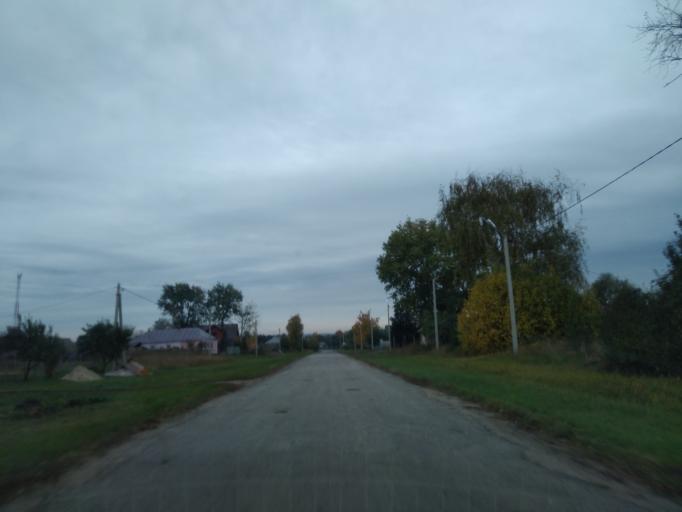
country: RU
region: Lipetsk
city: Zadonsk
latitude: 52.2950
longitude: 38.9448
